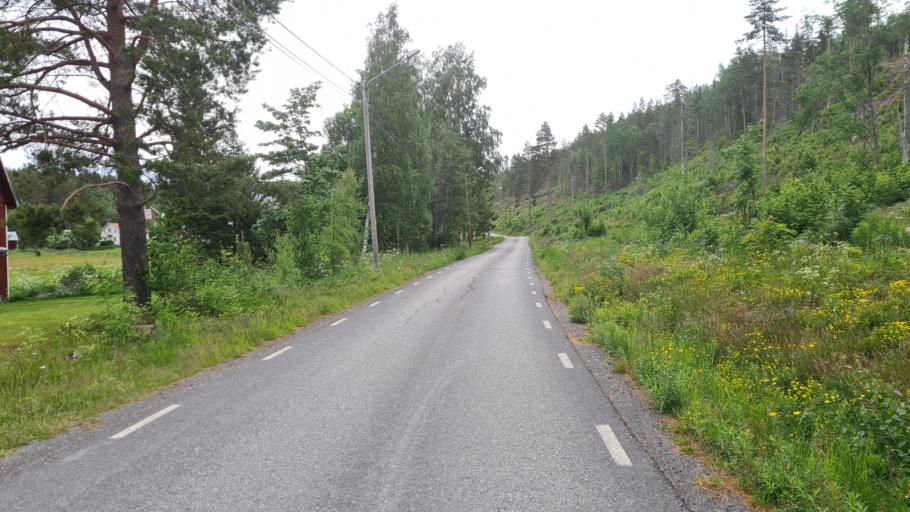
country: SE
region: Vaesternorrland
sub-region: Kramfors Kommun
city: Nordingra
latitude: 62.9761
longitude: 18.4261
